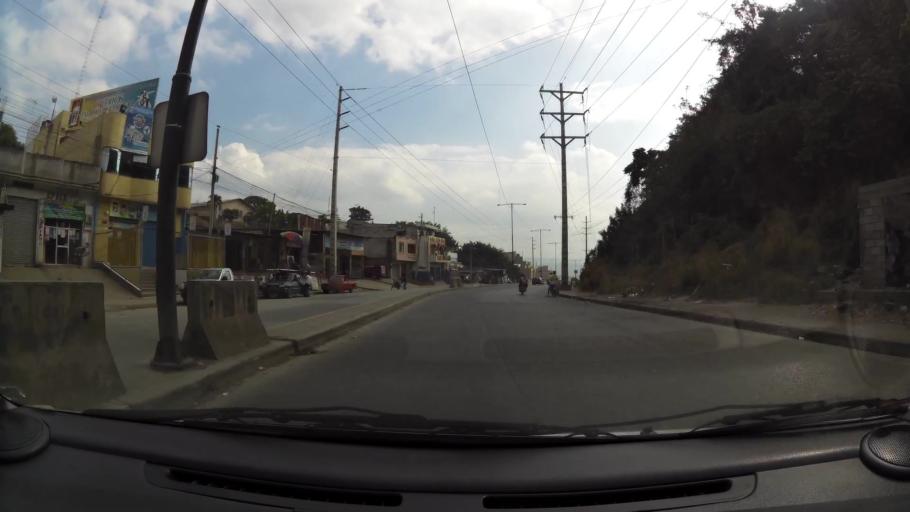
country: EC
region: Guayas
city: Santa Lucia
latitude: -2.1202
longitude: -79.9697
